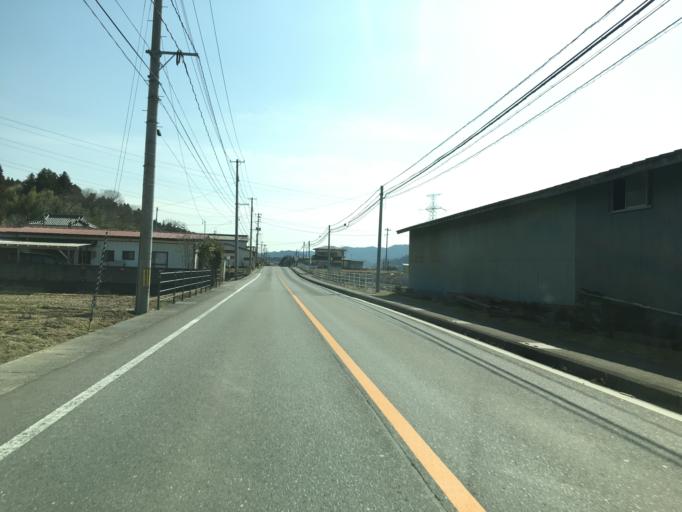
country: JP
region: Ibaraki
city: Daigo
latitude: 36.9034
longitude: 140.4182
